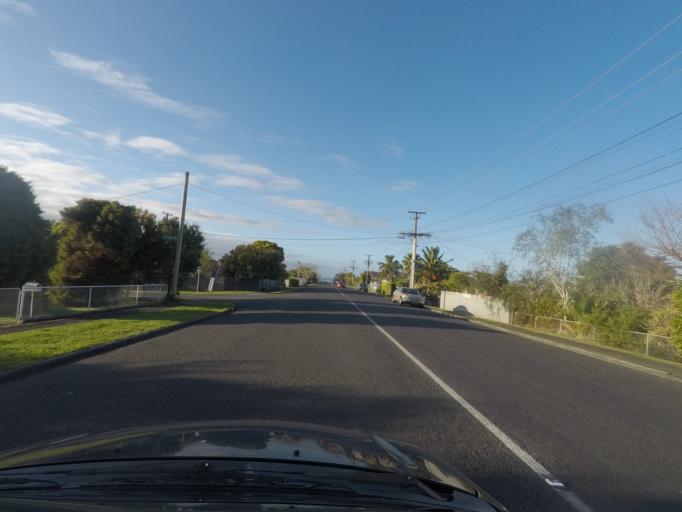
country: NZ
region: Auckland
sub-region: Auckland
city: Waitakere
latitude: -36.9152
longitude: 174.6580
